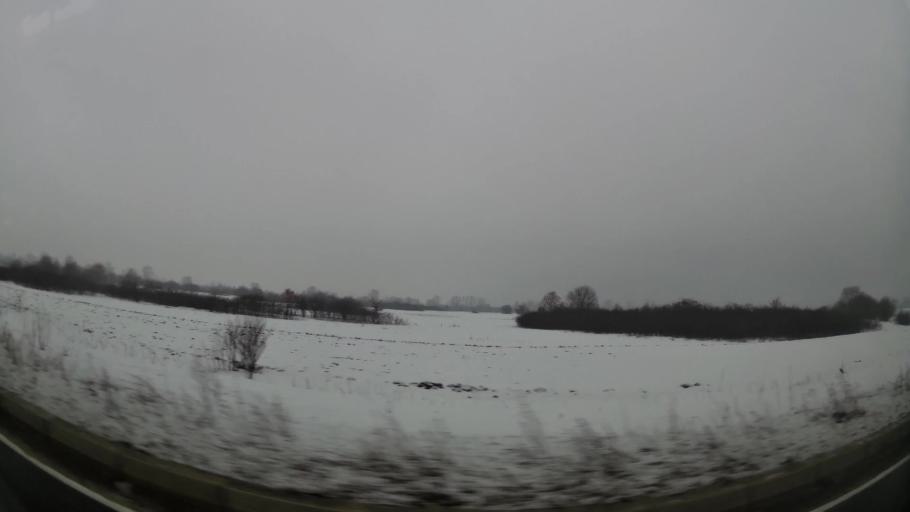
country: RS
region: Central Serbia
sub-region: Belgrade
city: Cukarica
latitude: 44.7508
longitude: 20.3766
